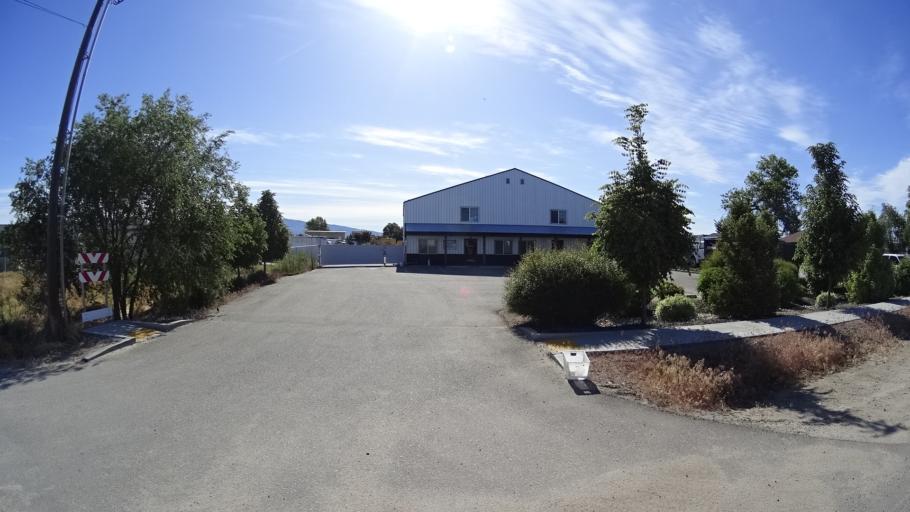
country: US
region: Idaho
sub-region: Ada County
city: Garden City
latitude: 43.5680
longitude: -116.2597
